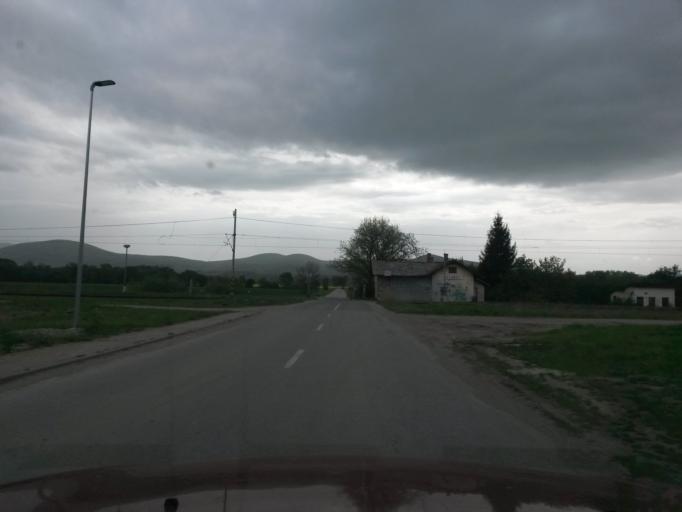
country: HU
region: Borsod-Abauj-Zemplen
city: Gonc
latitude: 48.5447
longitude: 21.2753
